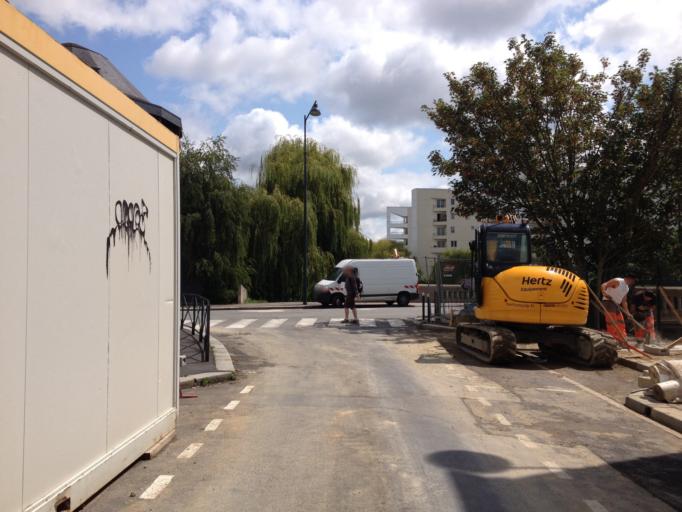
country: FR
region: Brittany
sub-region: Departement d'Ille-et-Vilaine
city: Rennes
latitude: 48.1078
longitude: -1.6662
